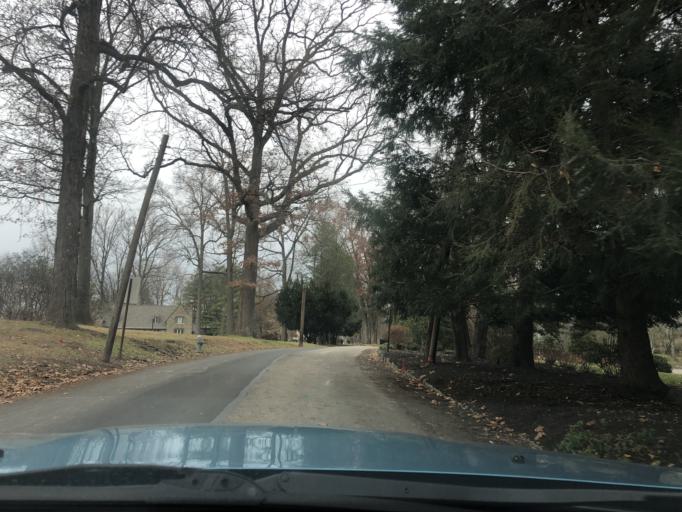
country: US
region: Pennsylvania
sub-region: Delaware County
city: Radnor
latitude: 40.0390
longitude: -75.3496
